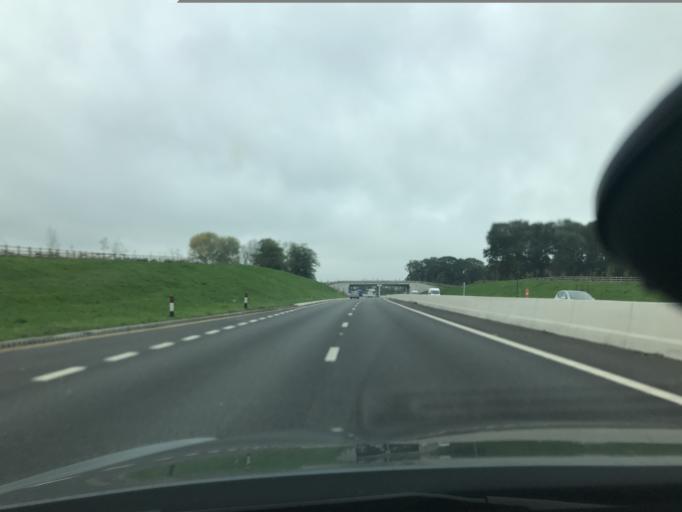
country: GB
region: England
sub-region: Cheshire East
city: Mere
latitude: 53.3352
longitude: -2.4187
